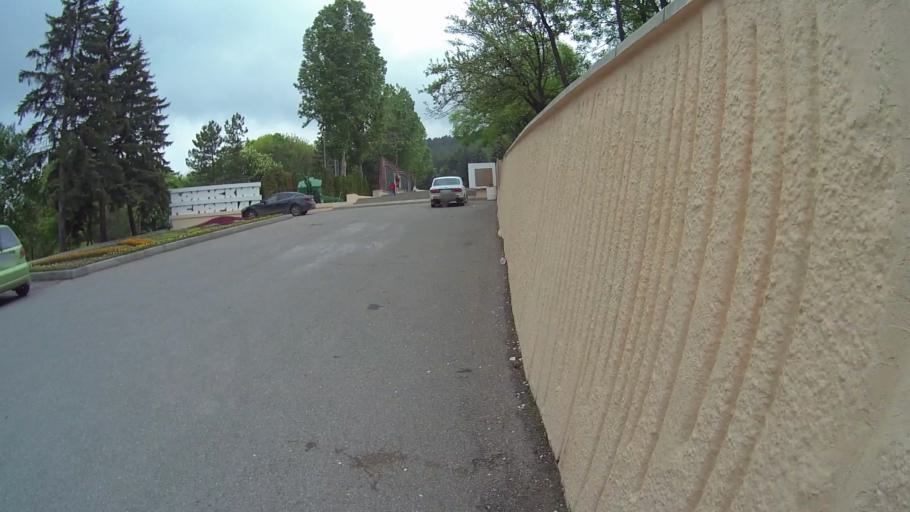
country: RU
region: Stavropol'skiy
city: Pyatigorsk
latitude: 44.0454
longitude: 43.0758
